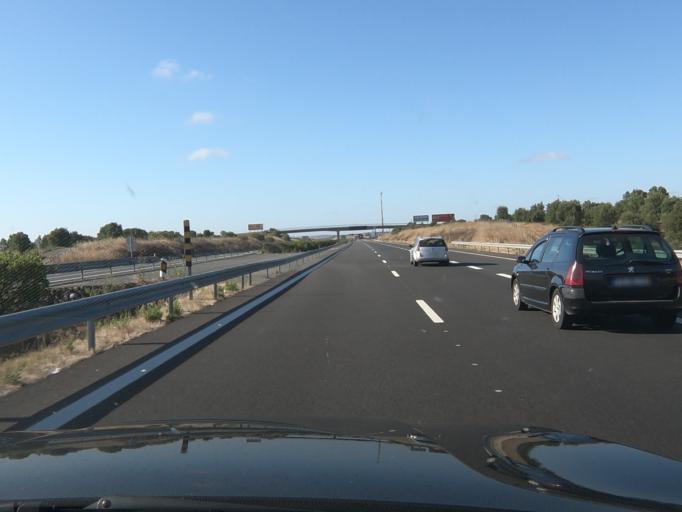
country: PT
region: Beja
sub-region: Aljustrel
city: Aljustrel
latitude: 37.9205
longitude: -8.2428
